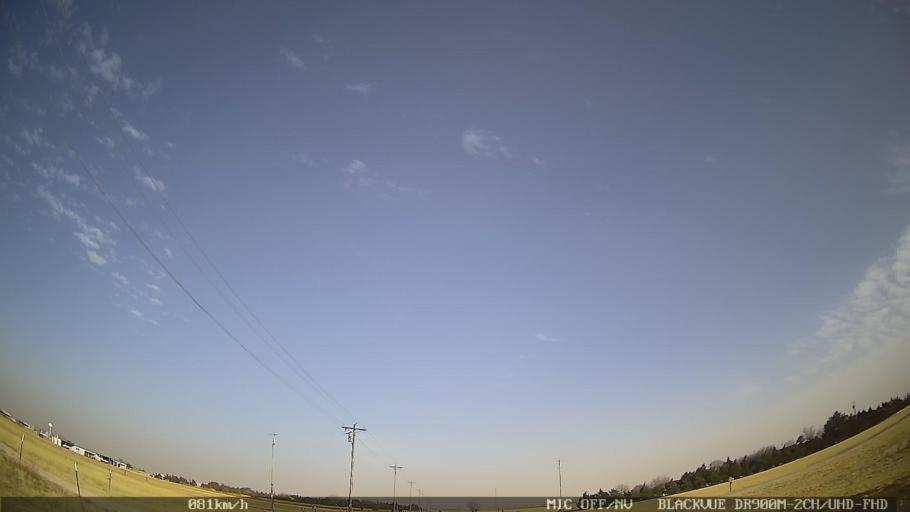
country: US
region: New Mexico
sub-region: Curry County
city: Texico
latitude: 34.4190
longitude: -103.0949
